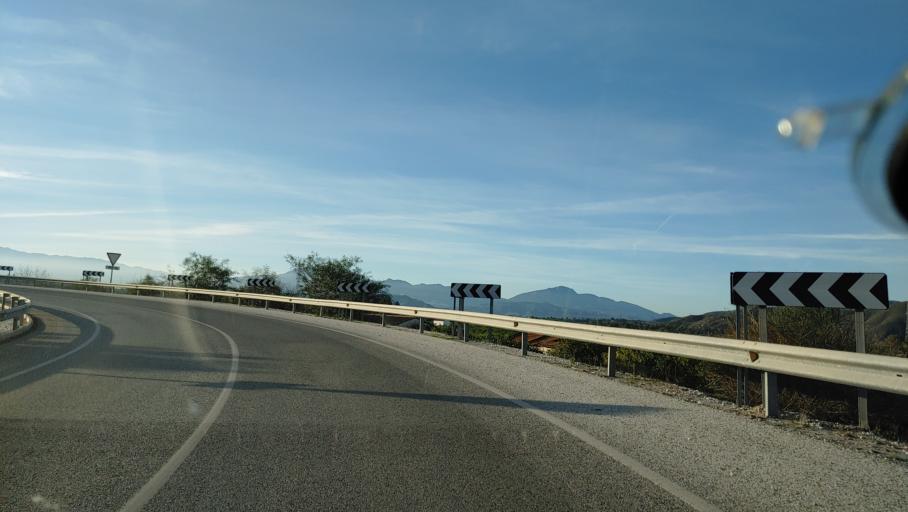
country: ES
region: Andalusia
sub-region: Provincia de Malaga
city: Cartama
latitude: 36.7169
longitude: -4.6464
